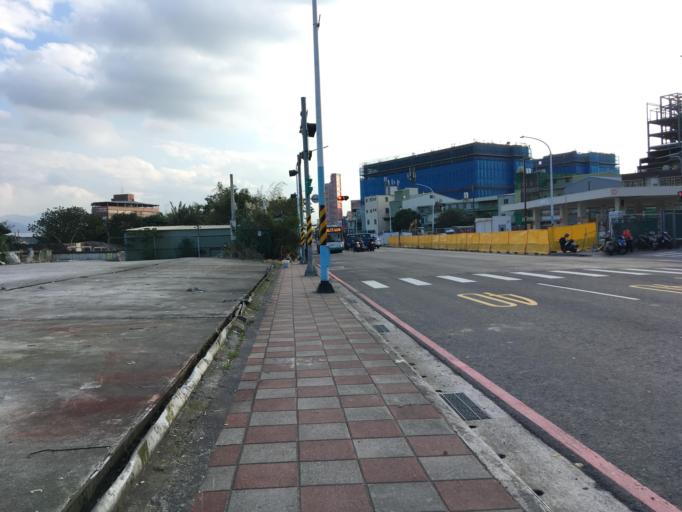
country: TW
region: Taipei
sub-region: Taipei
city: Banqiao
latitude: 25.0270
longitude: 121.4350
